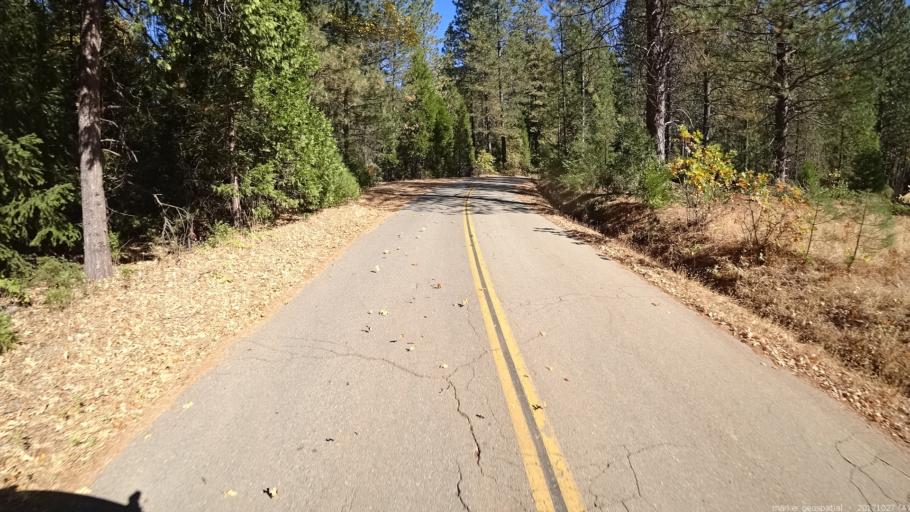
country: US
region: California
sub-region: Shasta County
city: Shingletown
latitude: 40.7370
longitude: -121.9494
